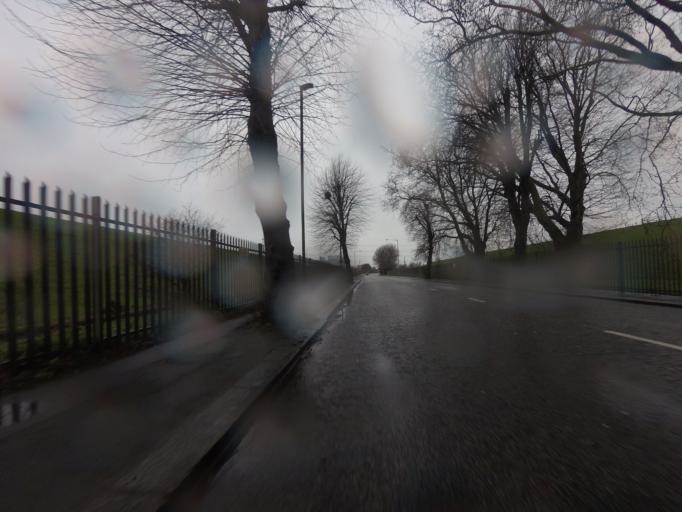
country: GB
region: England
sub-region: Greater London
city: Walthamstow
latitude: 51.6397
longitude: -0.0239
